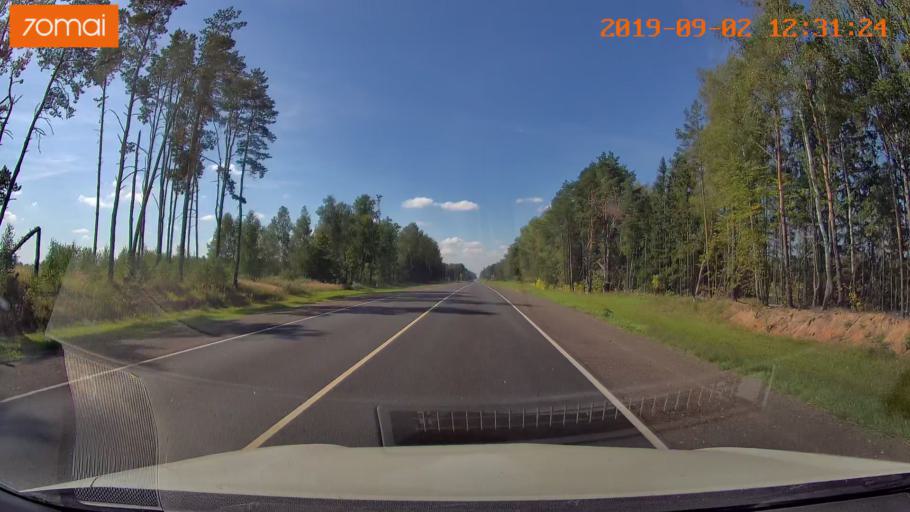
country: RU
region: Smolensk
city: Shumyachi
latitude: 53.8249
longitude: 32.4512
